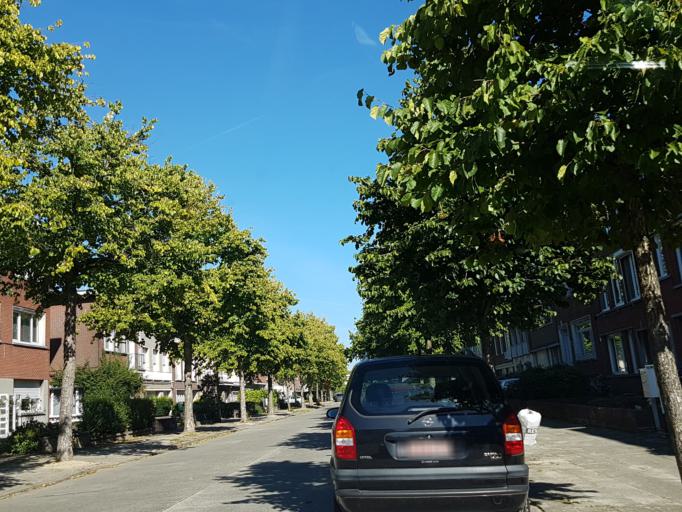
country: BE
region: Flanders
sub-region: Provincie Antwerpen
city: Mortsel
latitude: 51.1762
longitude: 4.4288
